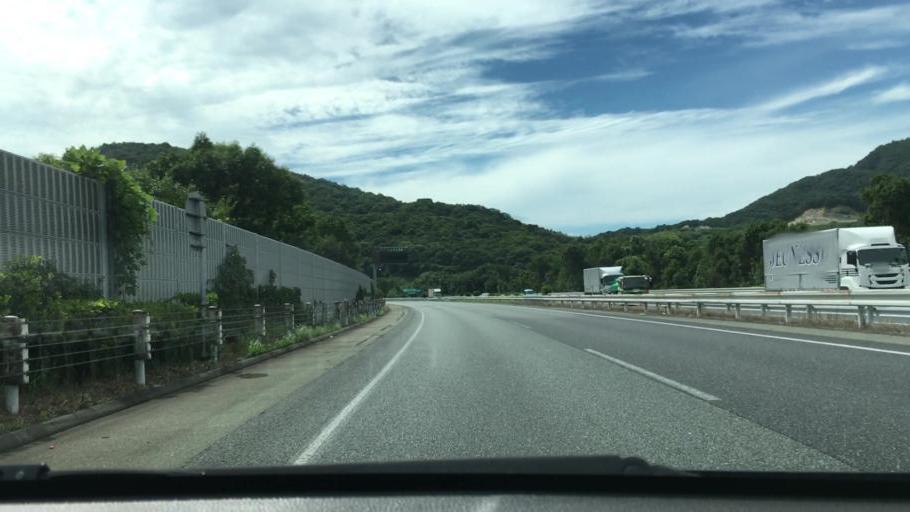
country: JP
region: Yamaguchi
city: Hofu
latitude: 34.0686
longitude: 131.6005
